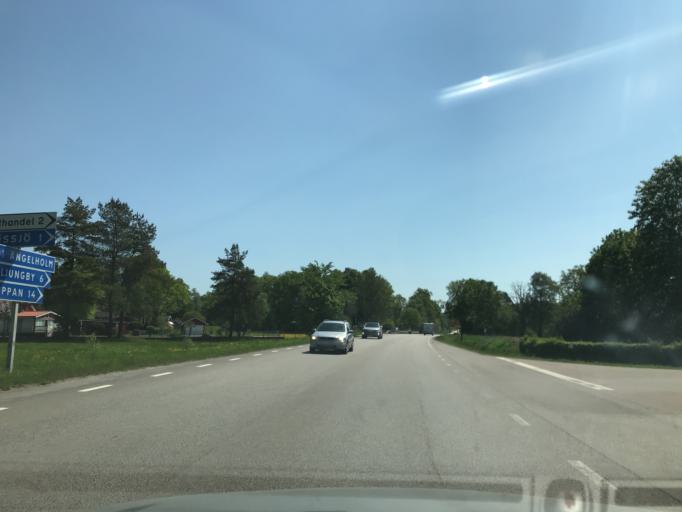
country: SE
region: Skane
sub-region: Angelholms Kommun
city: Munka-Ljungby
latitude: 56.2411
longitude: 13.0287
